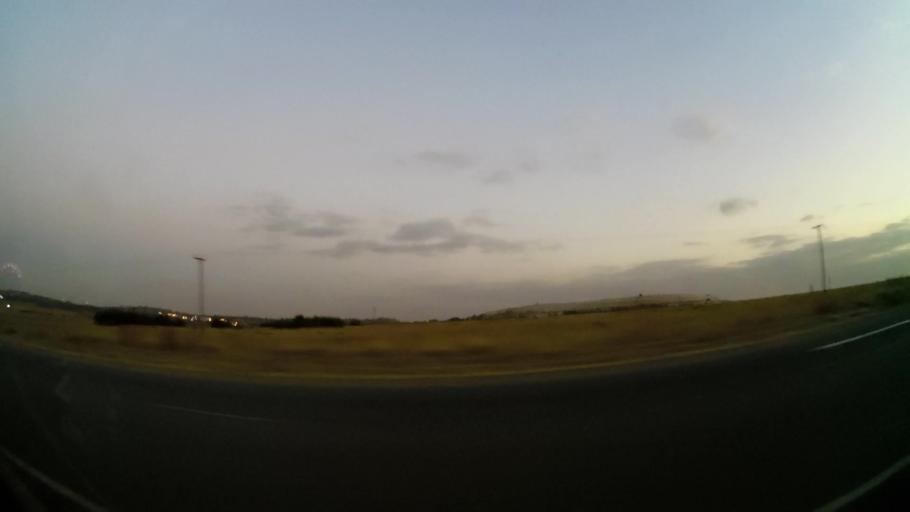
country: ZA
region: Gauteng
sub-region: West Rand District Municipality
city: Krugersdorp
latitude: -26.1101
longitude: 27.7106
